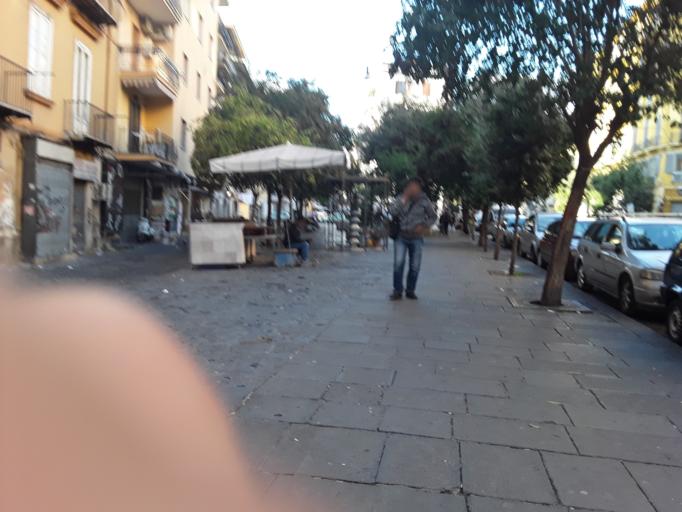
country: IT
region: Campania
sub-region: Provincia di Napoli
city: Napoli
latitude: 40.8572
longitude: 14.2672
